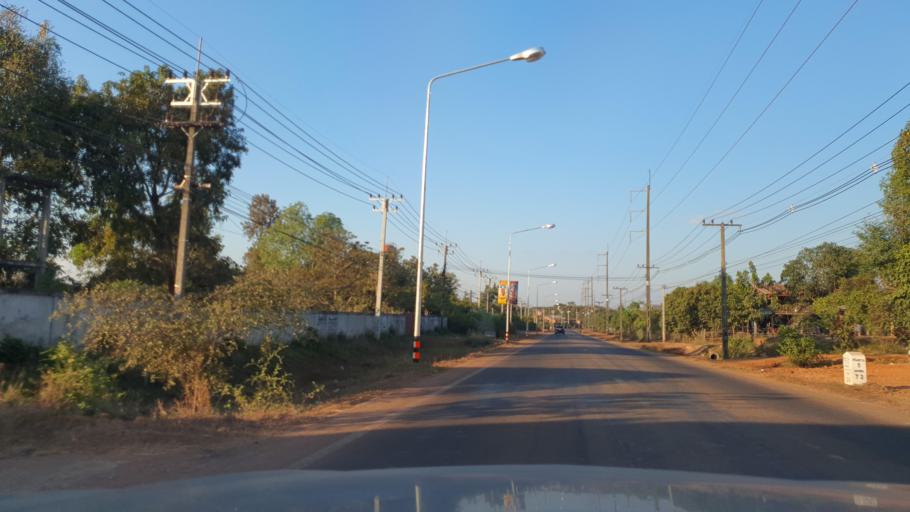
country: TH
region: Nakhon Phanom
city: Si Songkhram
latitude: 17.5821
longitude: 104.2330
